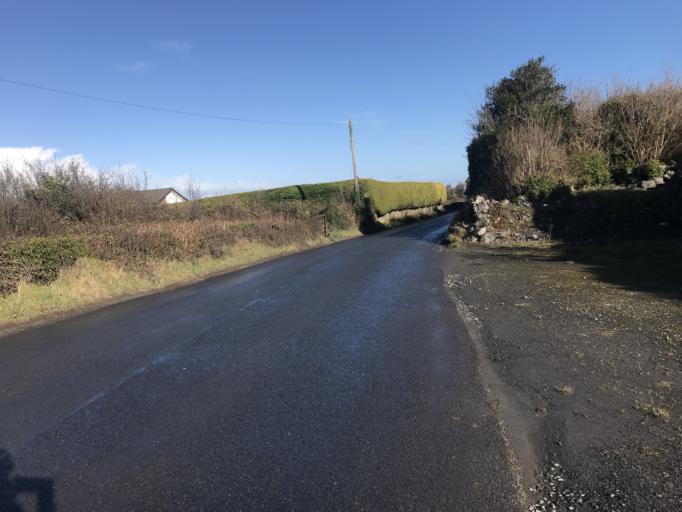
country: IE
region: Connaught
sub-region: County Galway
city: Gaillimh
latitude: 53.3040
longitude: -9.0202
